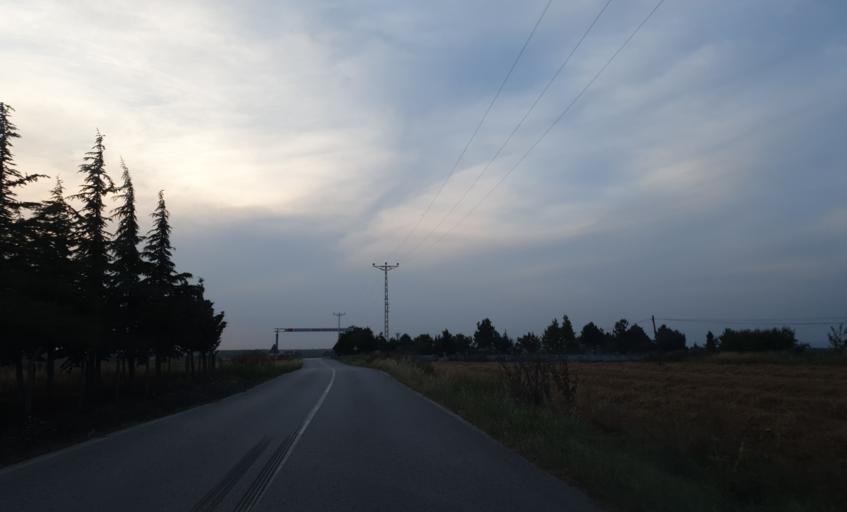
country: TR
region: Kirklareli
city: Buyukkaristiran
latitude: 41.3503
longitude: 27.6099
